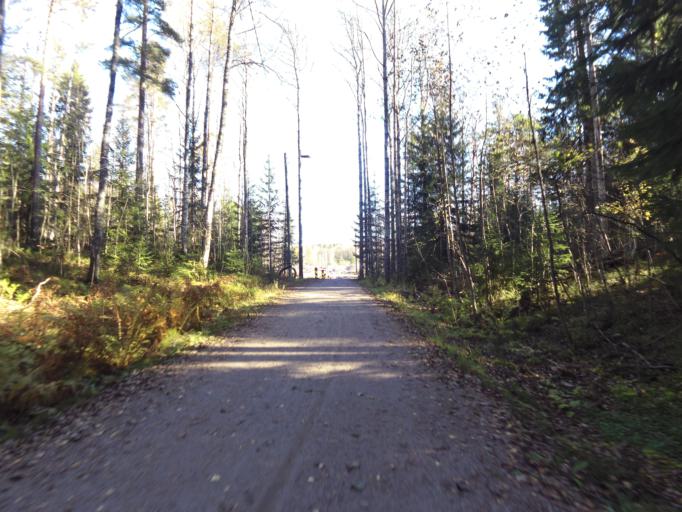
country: FI
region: Uusimaa
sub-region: Helsinki
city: Kauniainen
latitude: 60.1777
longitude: 24.7115
